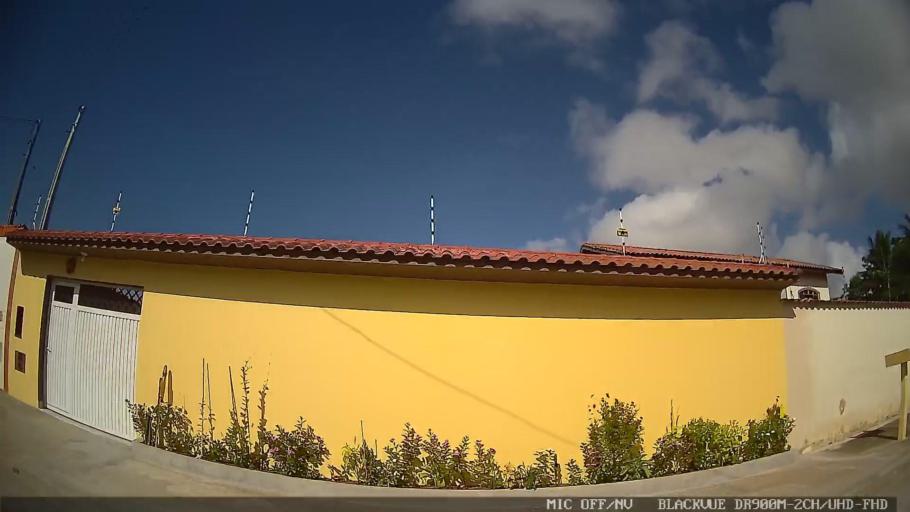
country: BR
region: Sao Paulo
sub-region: Peruibe
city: Peruibe
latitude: -24.2758
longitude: -46.9385
